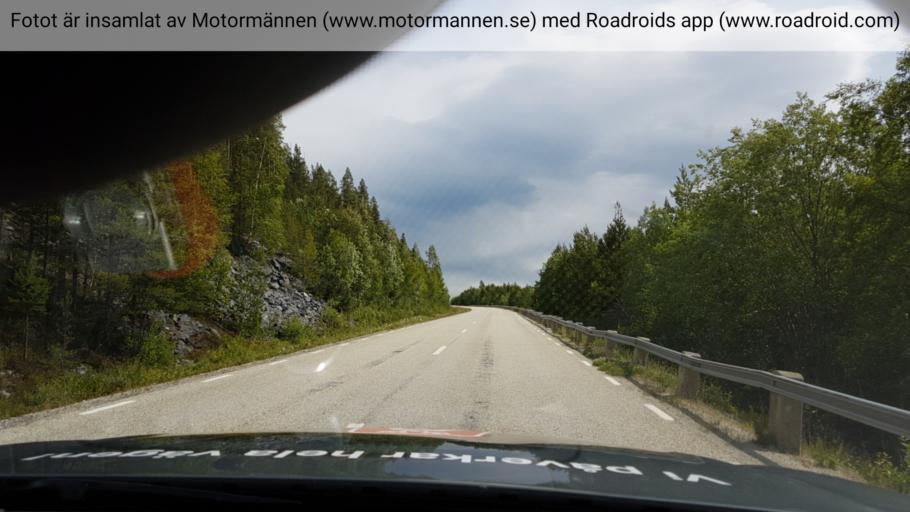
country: SE
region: Jaemtland
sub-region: Are Kommun
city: Jarpen
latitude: 62.8048
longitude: 13.5453
